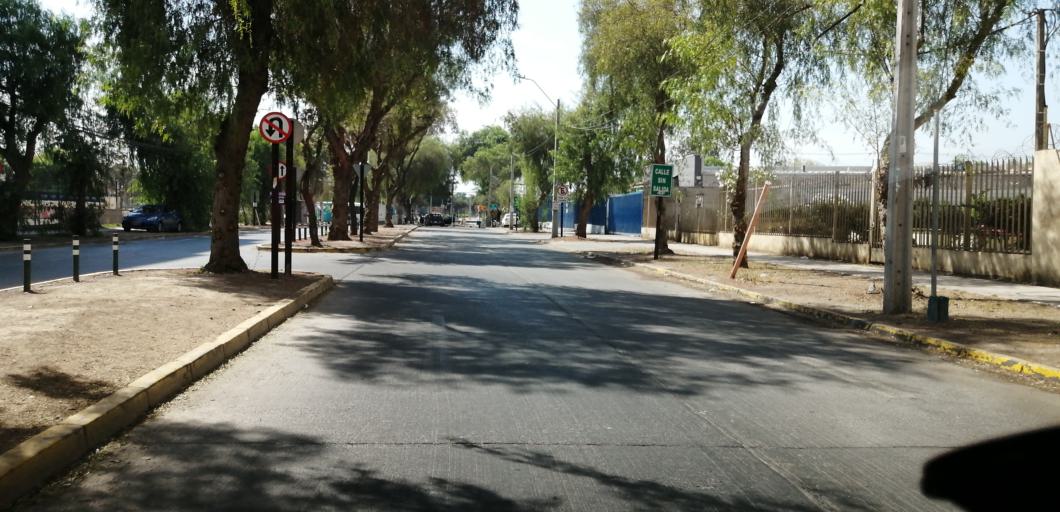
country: CL
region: Santiago Metropolitan
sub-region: Provincia de Santiago
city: Lo Prado
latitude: -33.4552
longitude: -70.7402
